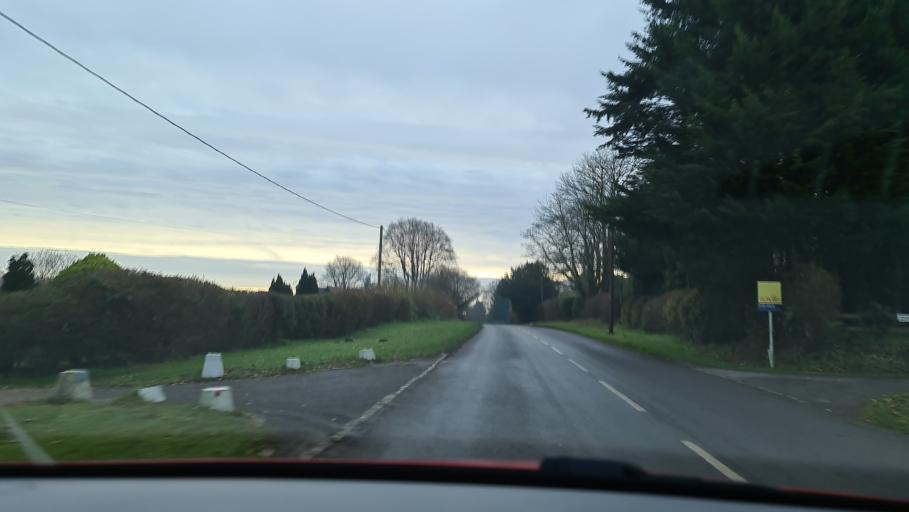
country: GB
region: England
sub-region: Buckinghamshire
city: Great Missenden
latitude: 51.7101
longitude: -0.7266
